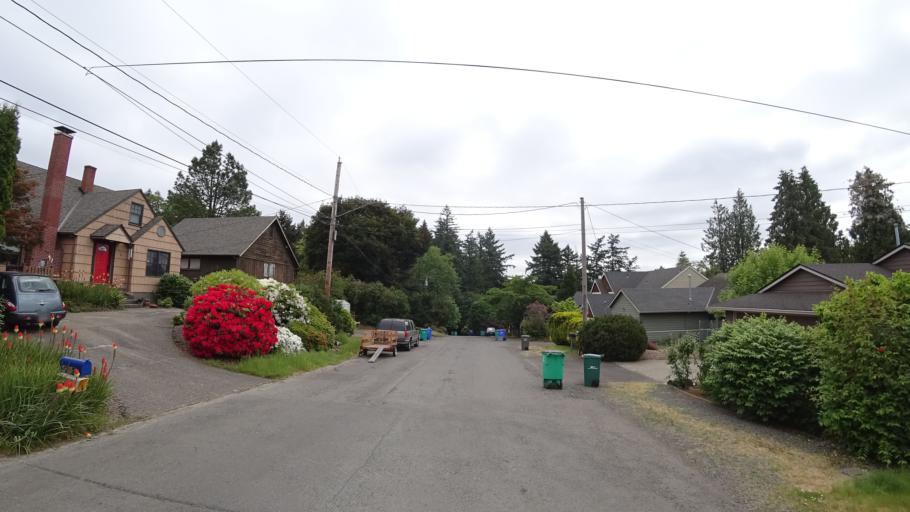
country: US
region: Oregon
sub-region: Washington County
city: Garden Home-Whitford
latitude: 45.4554
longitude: -122.7240
